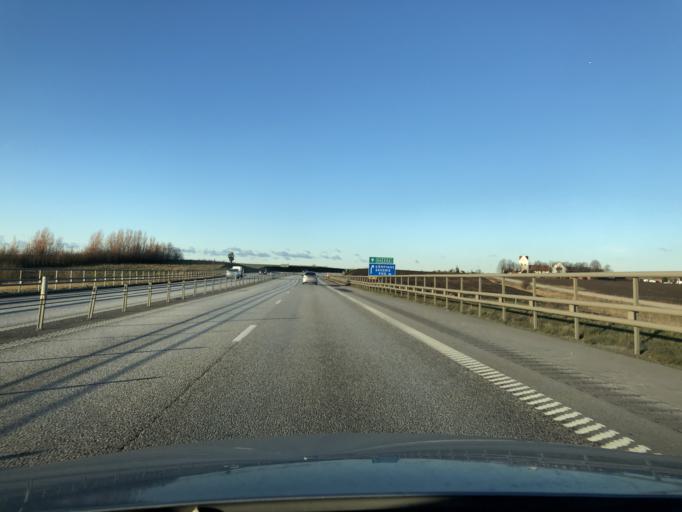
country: SE
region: Skane
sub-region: Trelleborgs Kommun
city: Skare
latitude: 55.3996
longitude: 13.0667
